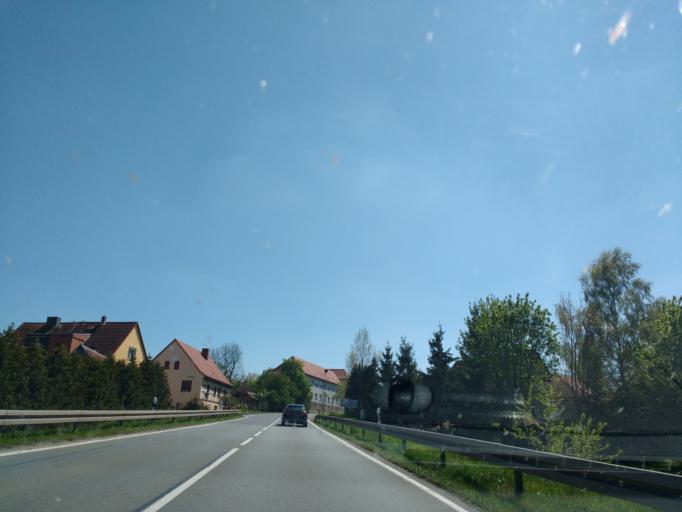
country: DE
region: Saxony-Anhalt
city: Deuben
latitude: 51.1134
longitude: 12.0850
